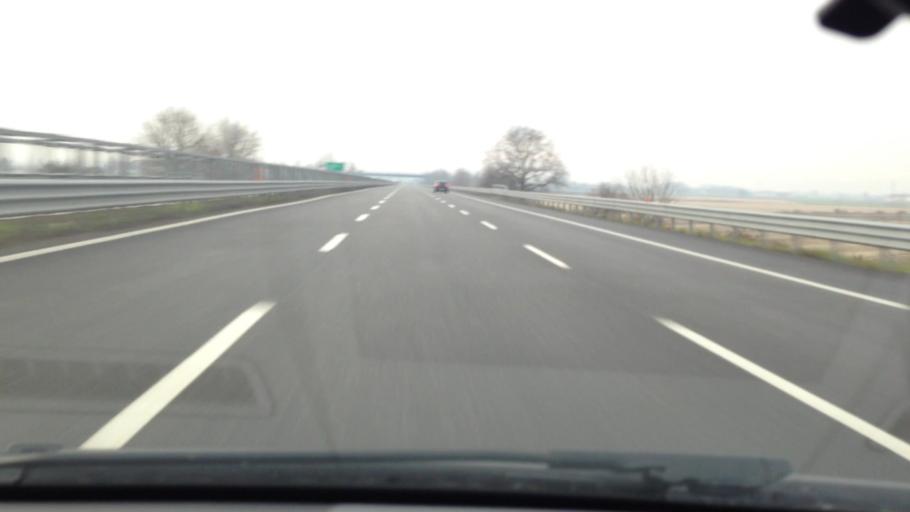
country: IT
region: Piedmont
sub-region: Provincia di Alessandria
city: Borgo San Martino
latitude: 45.0864
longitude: 8.5045
